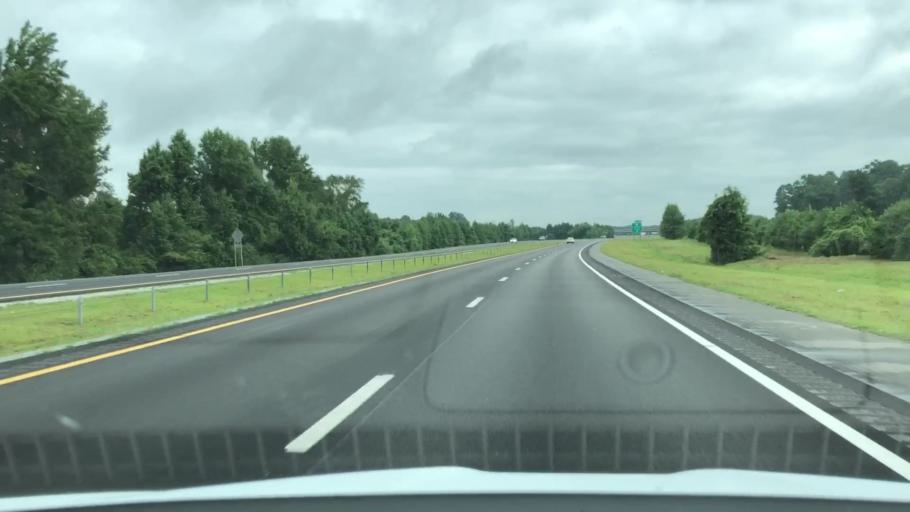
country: US
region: North Carolina
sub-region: Wayne County
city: Fremont
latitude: 35.5421
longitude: -77.9897
